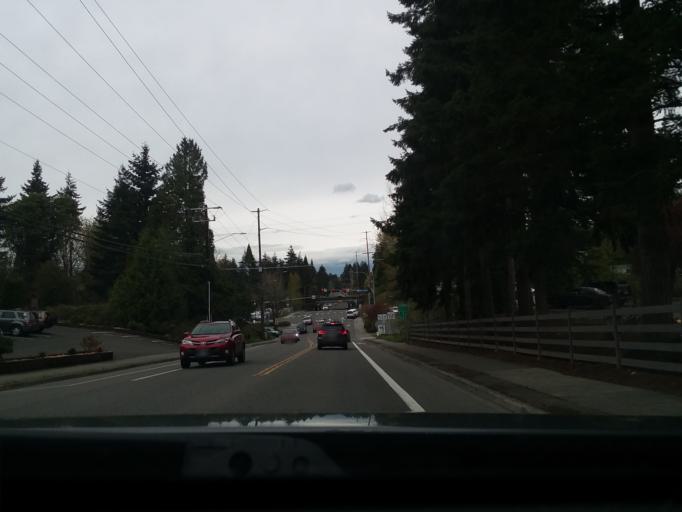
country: US
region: Washington
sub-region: Snohomish County
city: Mountlake Terrace
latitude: 47.8051
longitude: -122.3031
